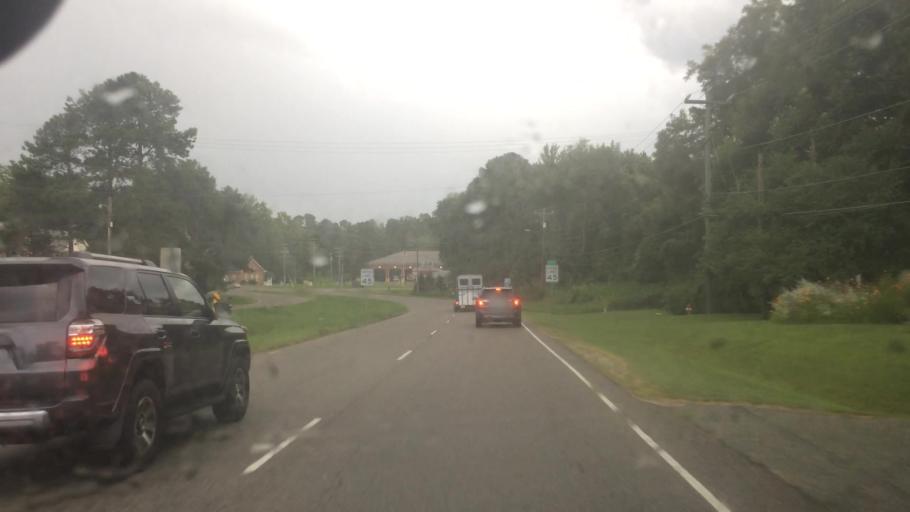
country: US
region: Virginia
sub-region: James City County
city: Williamsburg
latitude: 37.3840
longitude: -76.8061
